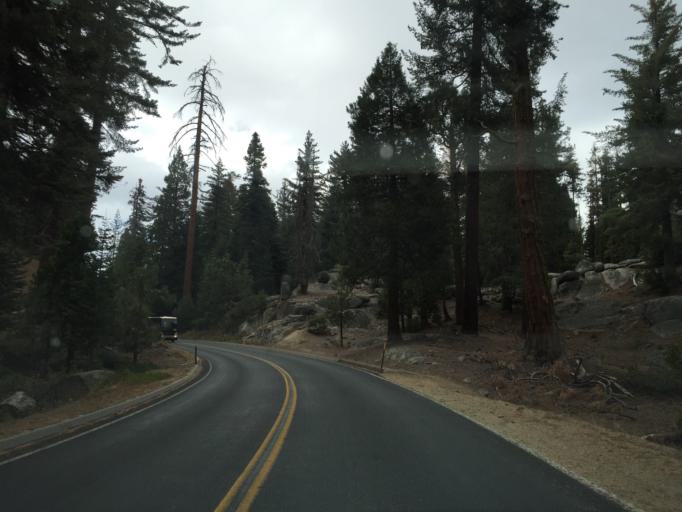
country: US
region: California
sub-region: Fresno County
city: Squaw Valley
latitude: 36.7318
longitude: -118.9603
